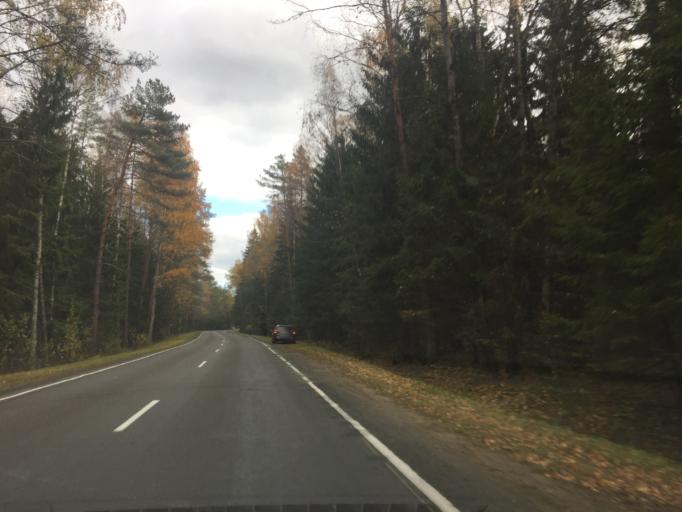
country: BY
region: Minsk
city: Svir
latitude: 54.9253
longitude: 26.4958
